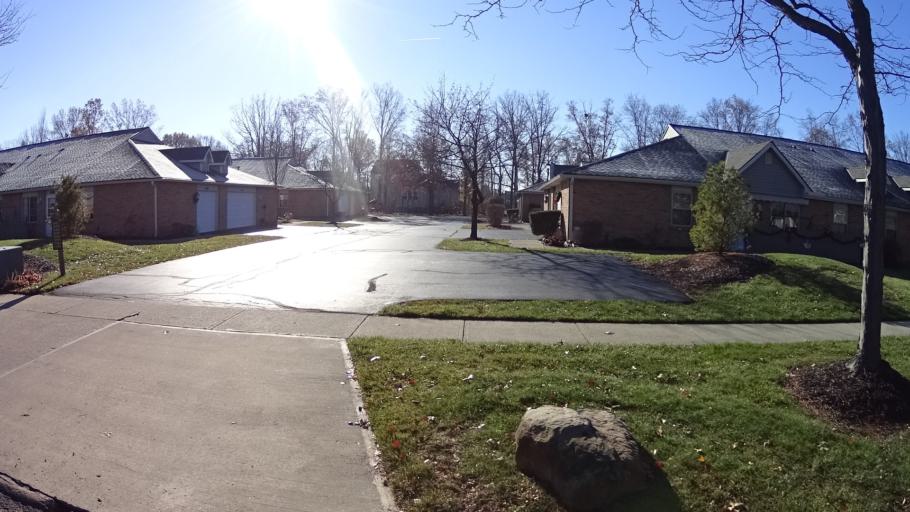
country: US
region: Ohio
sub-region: Lorain County
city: North Ridgeville
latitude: 41.4178
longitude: -82.0087
